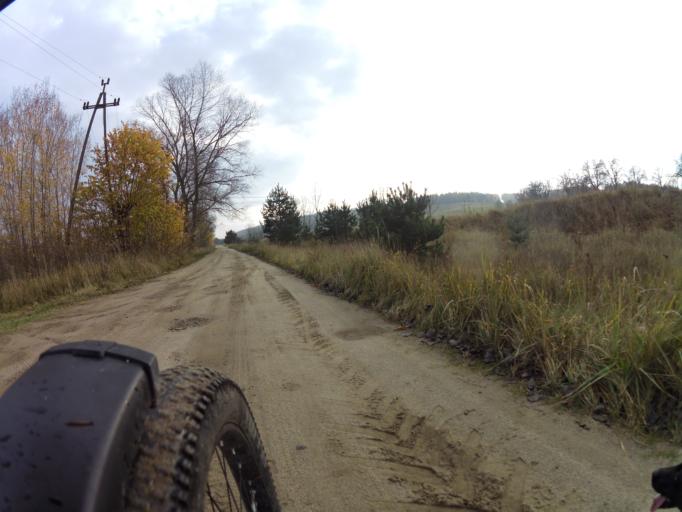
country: PL
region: Pomeranian Voivodeship
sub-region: Powiat wejherowski
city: Gniewino
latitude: 54.7093
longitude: 18.0991
